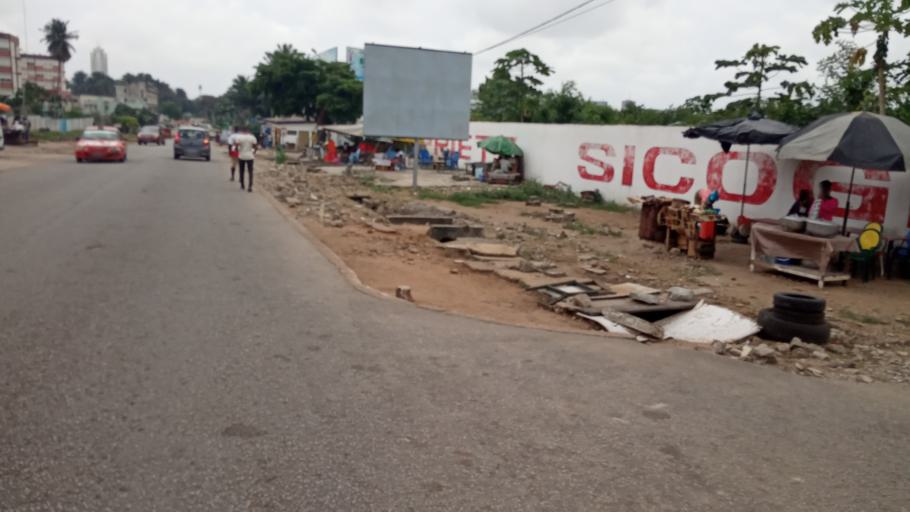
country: CI
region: Lagunes
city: Abidjan
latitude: 5.3397
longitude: -4.0049
